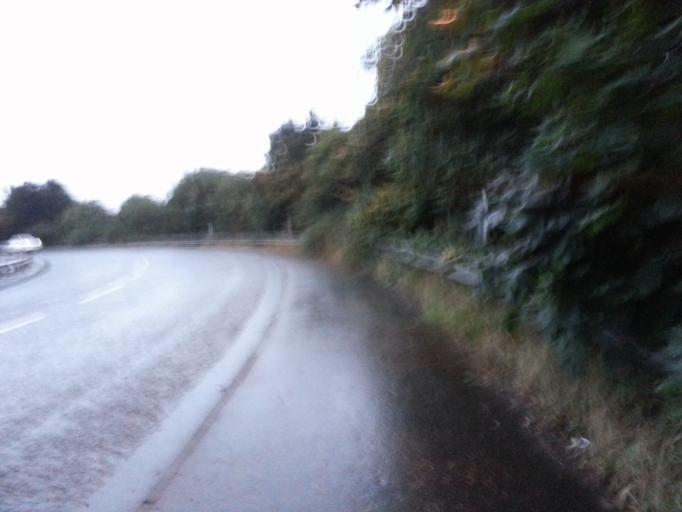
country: GB
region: Northern Ireland
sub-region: Newtownabbey District
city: Newtownabbey
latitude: 54.6302
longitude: -5.9220
